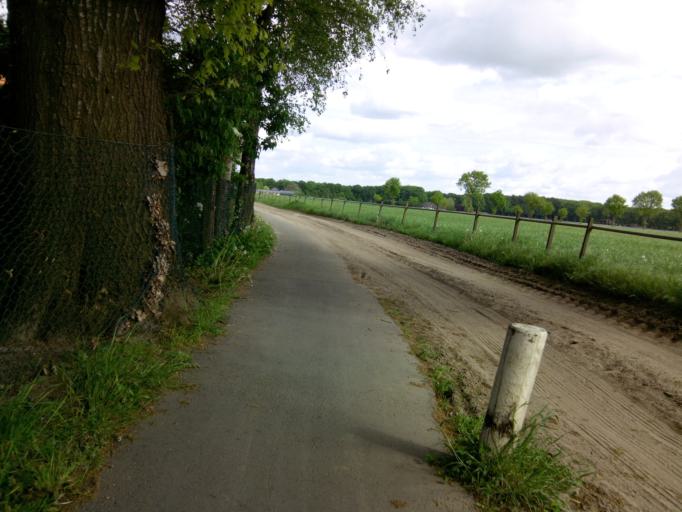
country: NL
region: Gelderland
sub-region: Gemeente Ede
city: Lunteren
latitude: 52.0686
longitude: 5.6451
